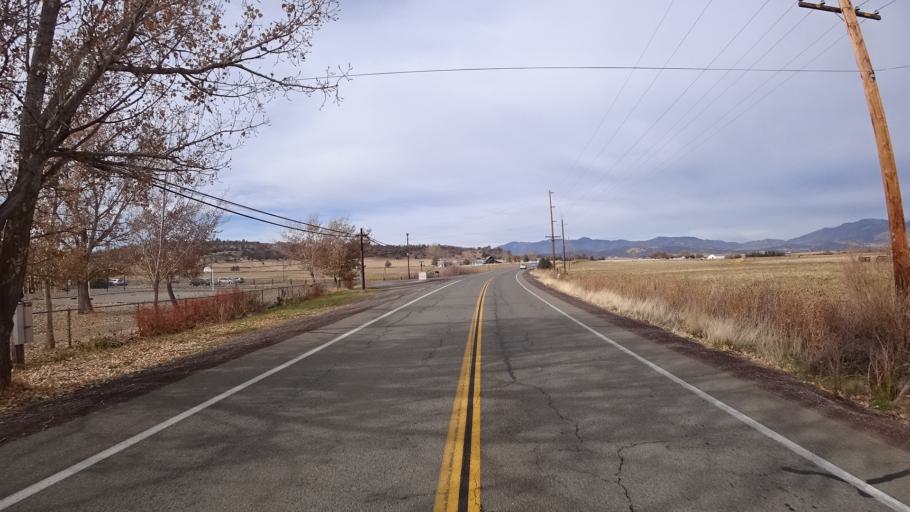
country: US
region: California
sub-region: Siskiyou County
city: Montague
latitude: 41.7055
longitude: -122.5633
